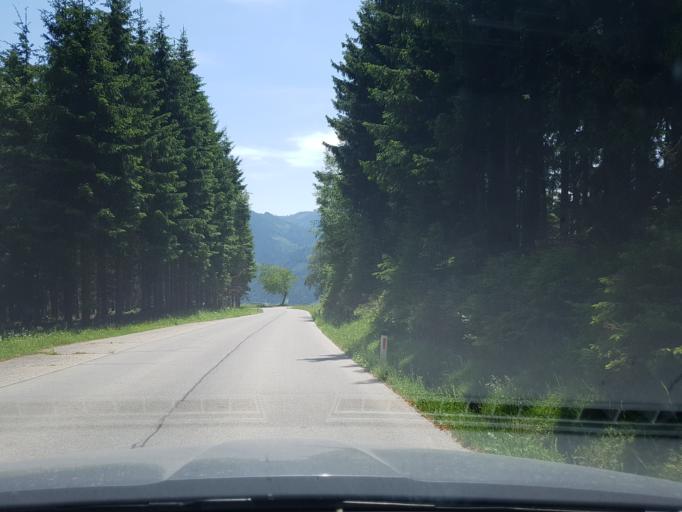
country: AT
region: Carinthia
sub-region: Politischer Bezirk Villach Land
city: Stockenboi
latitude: 46.7407
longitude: 13.5452
